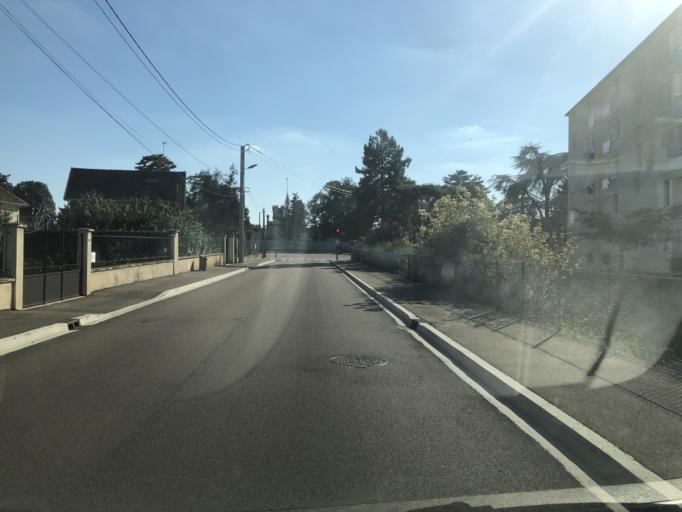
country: FR
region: Bourgogne
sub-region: Departement de l'Yonne
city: Auxerre
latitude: 47.7936
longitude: 3.5881
